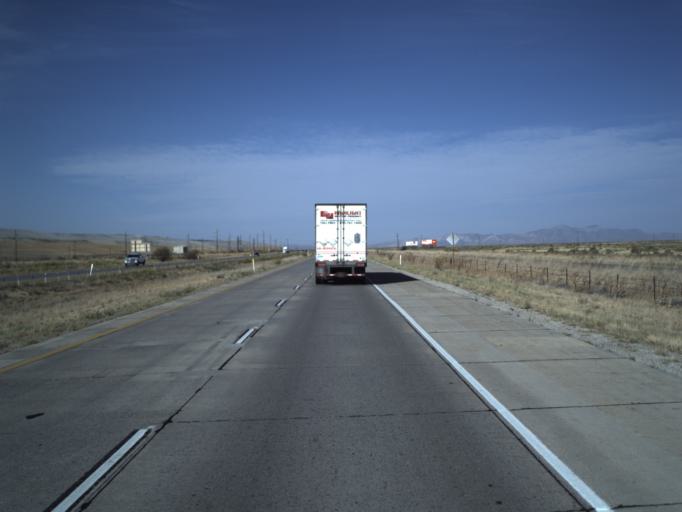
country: US
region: Utah
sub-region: Salt Lake County
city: Magna
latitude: 40.7711
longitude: -112.0874
